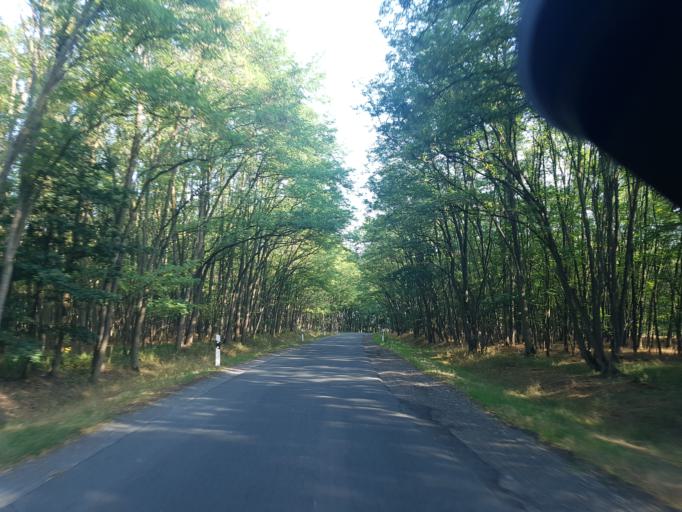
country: DE
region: Brandenburg
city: Niemegk
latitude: 52.0053
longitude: 12.6823
